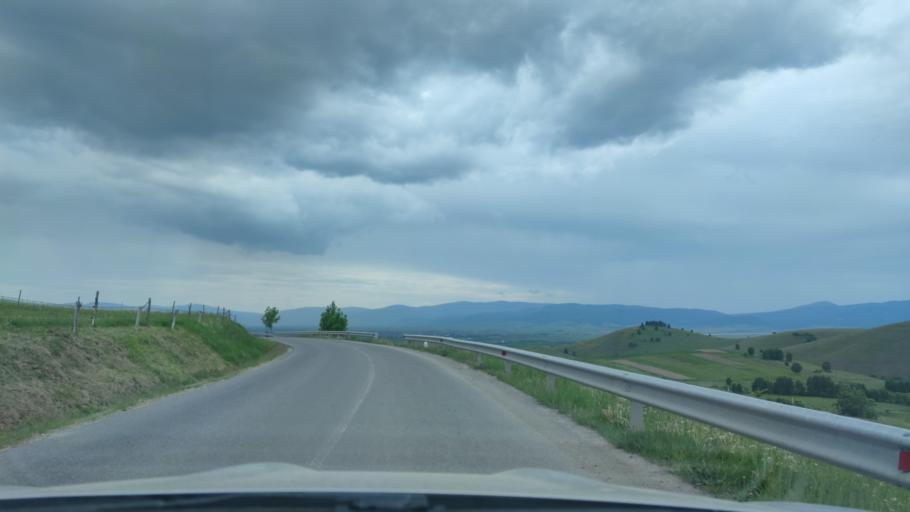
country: RO
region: Harghita
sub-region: Comuna Ditrau
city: Ditrau
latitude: 46.8518
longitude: 25.5053
